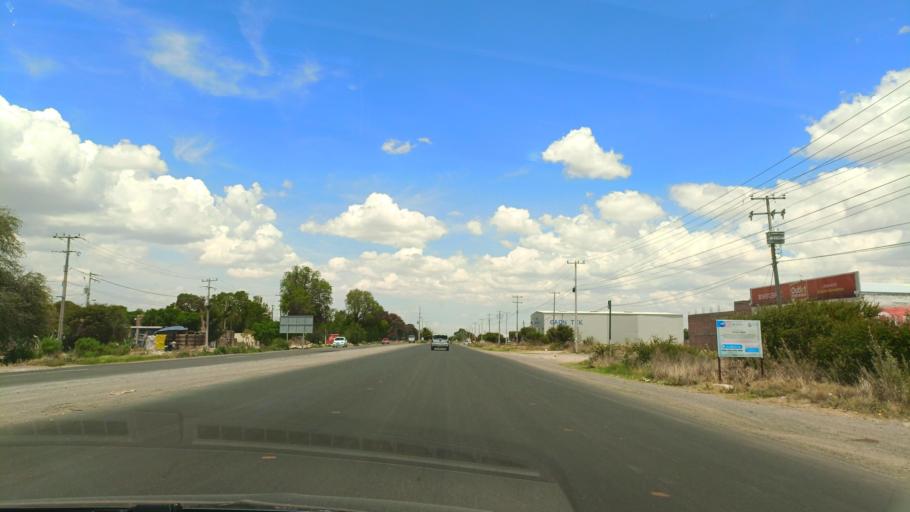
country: MX
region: Guanajuato
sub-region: San Luis de la Paz
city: San Ignacio
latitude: 21.2875
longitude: -100.5612
